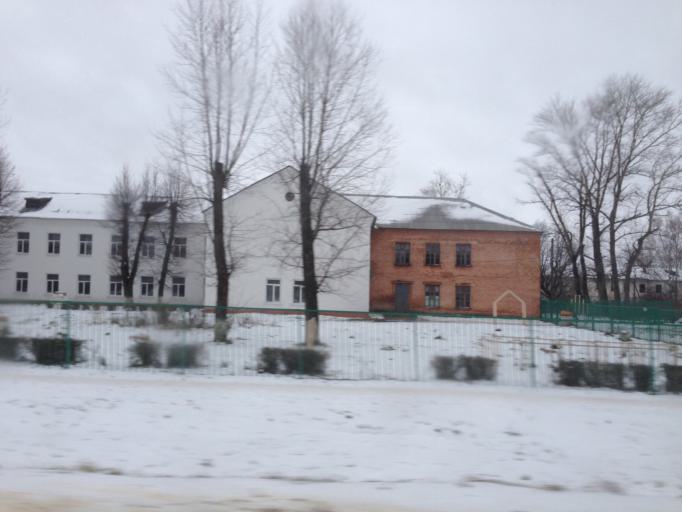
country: RU
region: Tula
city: Uzlovaya
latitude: 53.9982
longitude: 38.1285
